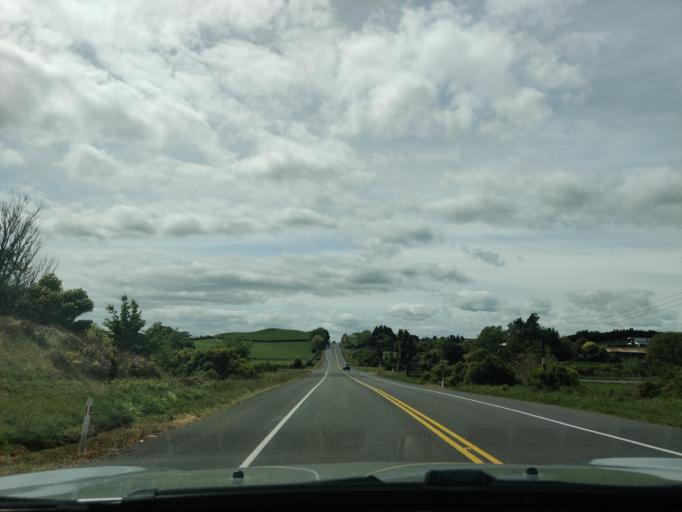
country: NZ
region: Taranaki
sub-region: New Plymouth District
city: New Plymouth
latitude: -39.1513
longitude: 174.1588
